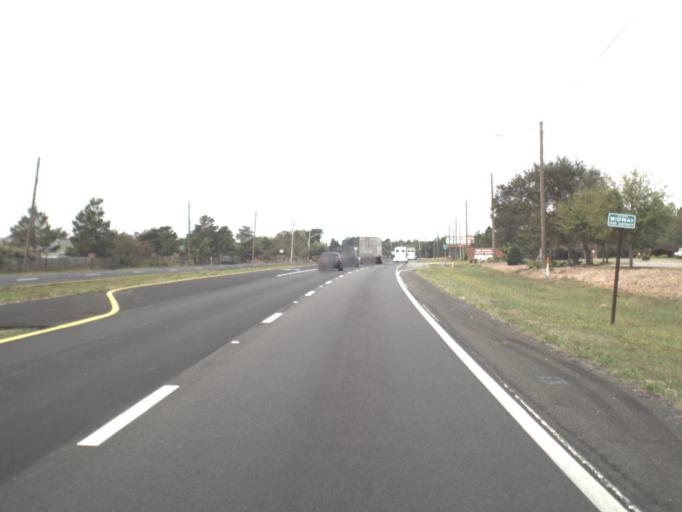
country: US
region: Florida
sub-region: Santa Rosa County
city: Woodlawn Beach
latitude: 30.4028
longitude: -86.9514
